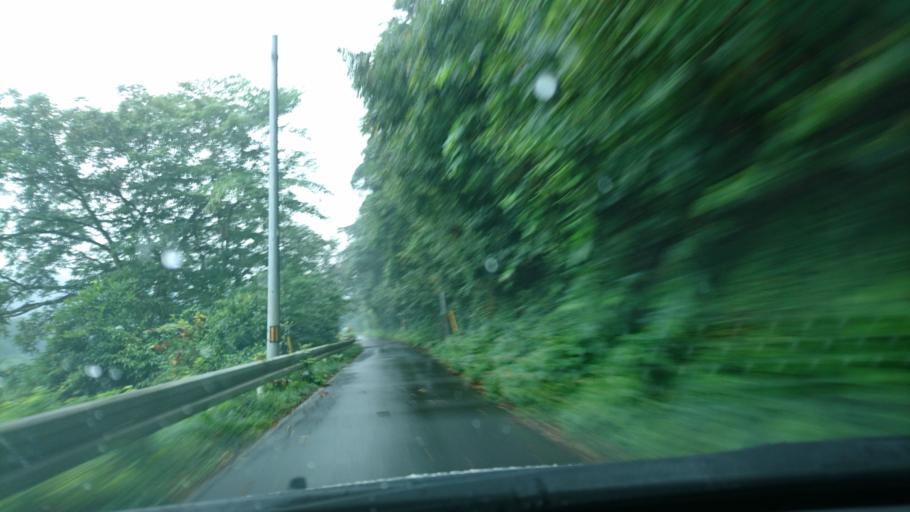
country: JP
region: Iwate
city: Ichinoseki
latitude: 38.8762
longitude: 141.2592
